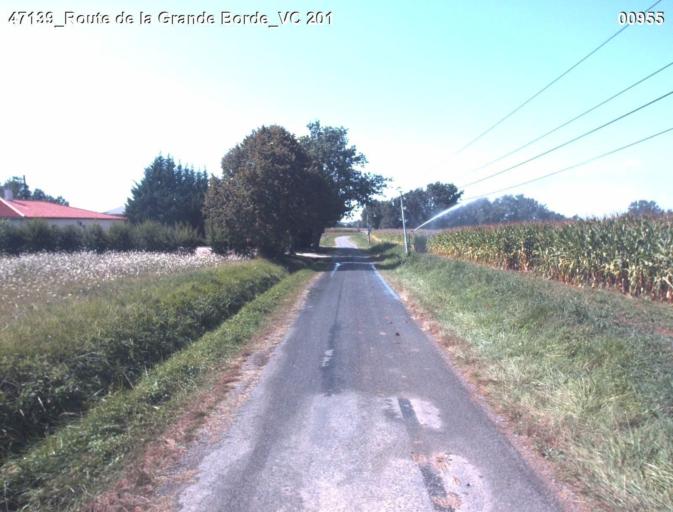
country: FR
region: Aquitaine
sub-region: Departement du Lot-et-Garonne
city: Nerac
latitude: 44.0700
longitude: 0.3905
